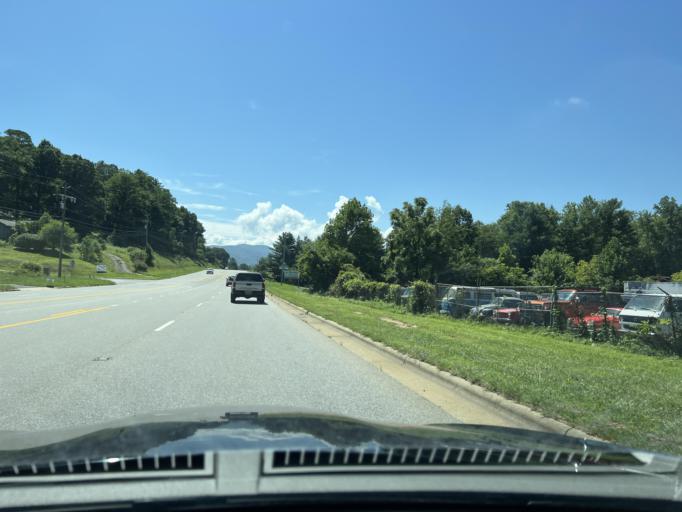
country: US
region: North Carolina
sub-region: Buncombe County
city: Fairview
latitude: 35.5431
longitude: -82.4419
